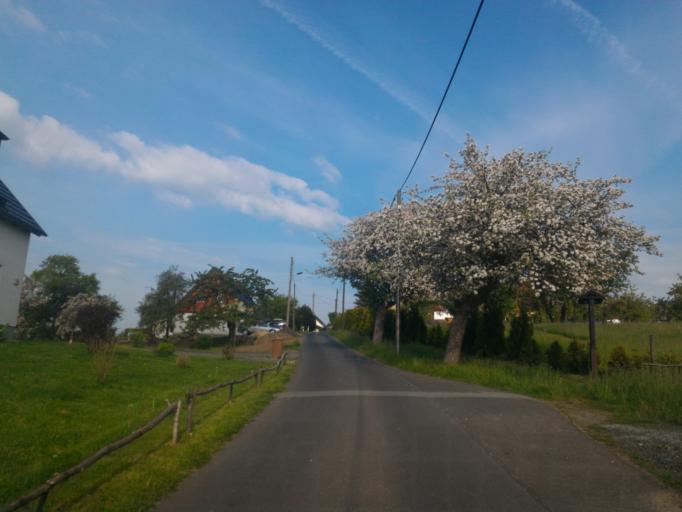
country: DE
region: Saxony
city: Leutersdorf
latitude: 50.9554
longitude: 14.6346
